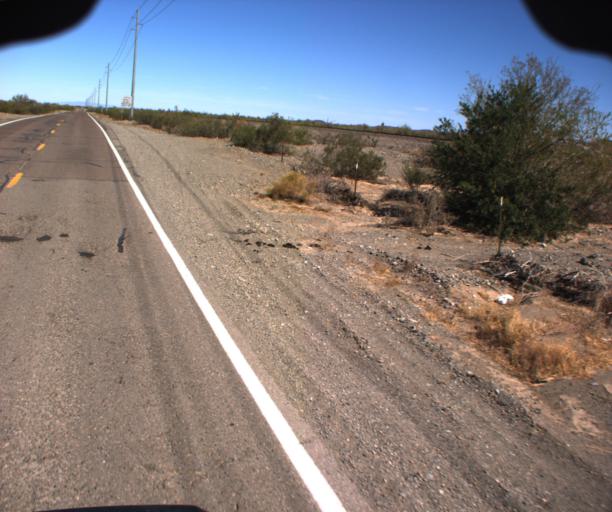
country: US
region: Arizona
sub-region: La Paz County
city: Salome
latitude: 33.7558
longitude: -113.7763
